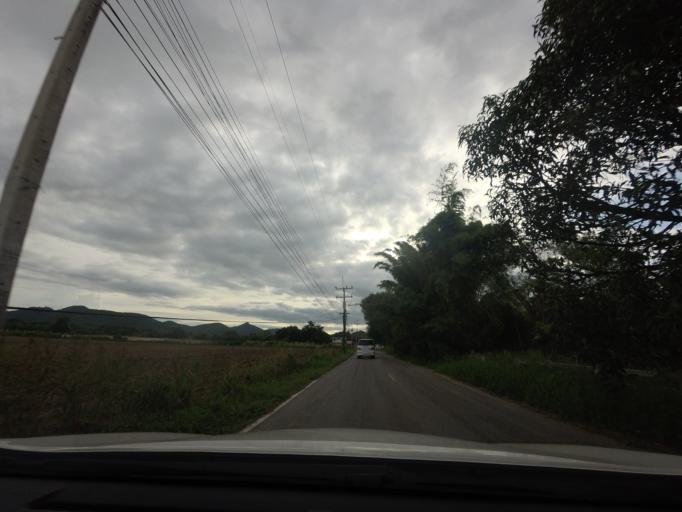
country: TH
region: Nakhon Ratchasima
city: Pak Chong
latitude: 14.6068
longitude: 101.4394
